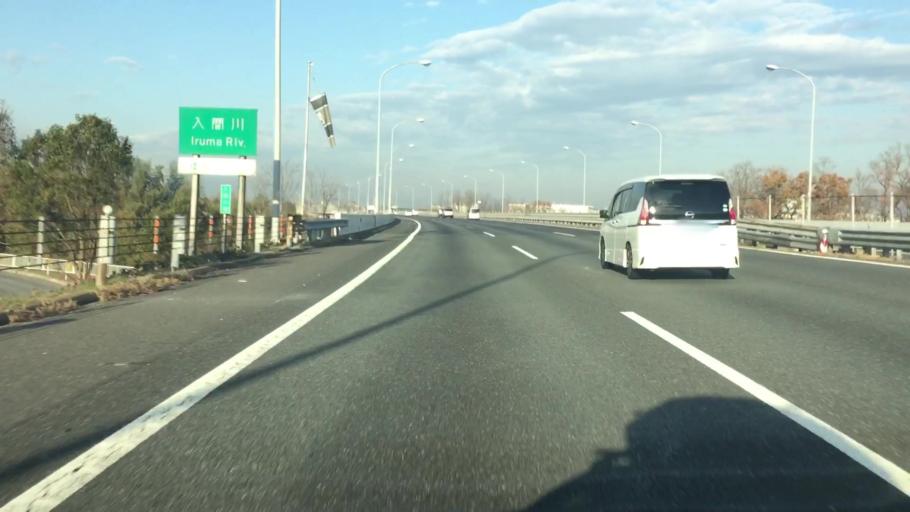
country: JP
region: Saitama
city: Kawagoe
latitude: 35.9100
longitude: 139.4452
